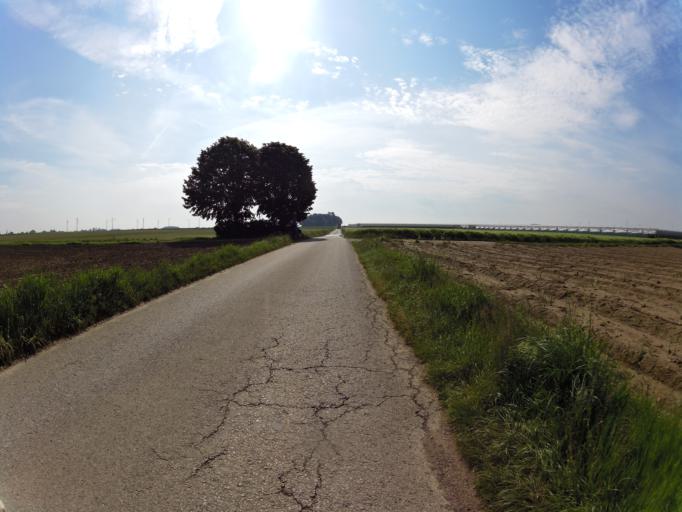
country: DE
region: North Rhine-Westphalia
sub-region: Regierungsbezirk Koln
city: Waldfeucht
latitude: 51.0677
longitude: 6.0091
